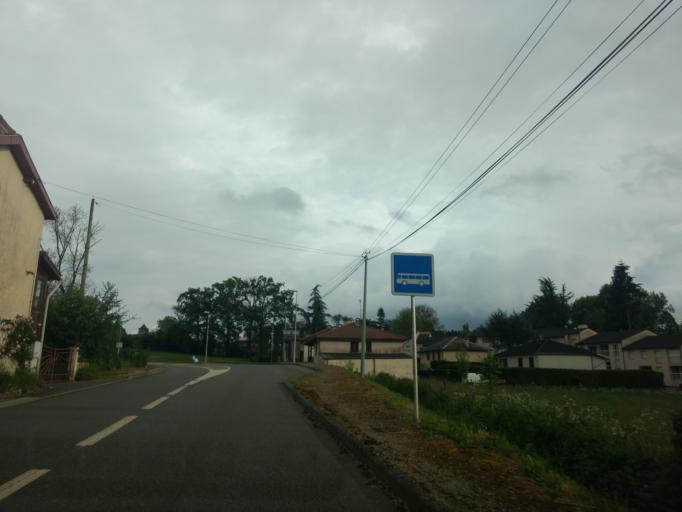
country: FR
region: Midi-Pyrenees
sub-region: Departement de l'Aveyron
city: Montbazens
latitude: 44.4818
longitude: 2.2252
